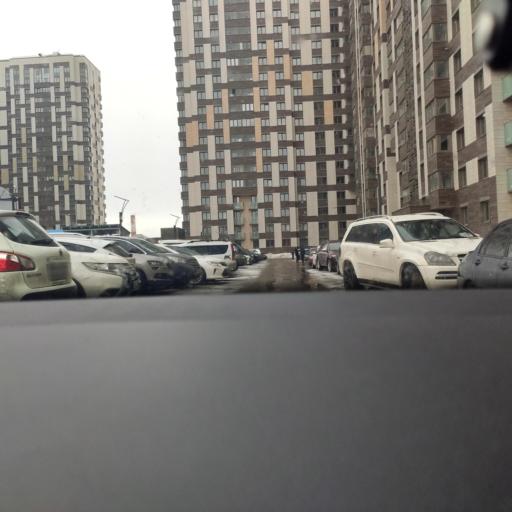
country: RU
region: Moscow
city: Novovladykino
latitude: 55.8490
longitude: 37.5793
